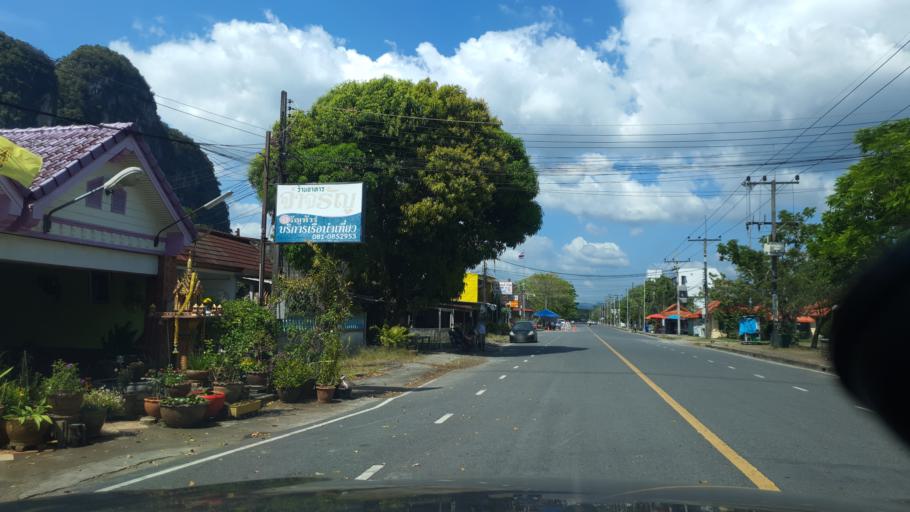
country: TH
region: Phangnga
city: Phang Nga
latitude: 8.3971
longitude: 98.5140
